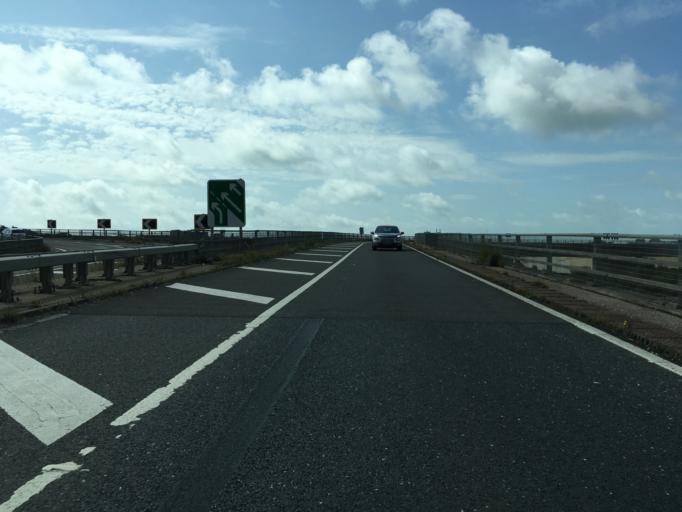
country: GB
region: England
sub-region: West Sussex
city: Shoreham-by-Sea
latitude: 50.8459
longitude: -0.2858
